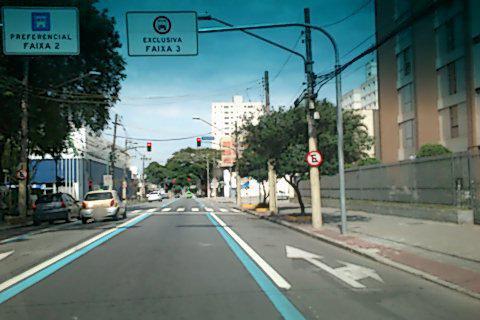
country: BR
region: Sao Paulo
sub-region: Sao Jose Dos Campos
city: Sao Jose dos Campos
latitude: -23.2002
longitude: -45.8925
